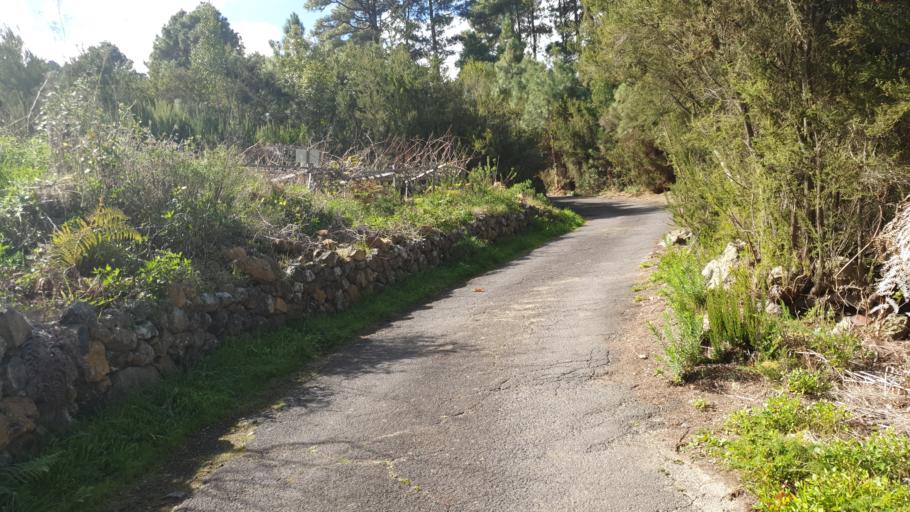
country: ES
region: Canary Islands
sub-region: Provincia de Santa Cruz de Tenerife
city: La Guancha
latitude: 28.3518
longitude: -16.6839
